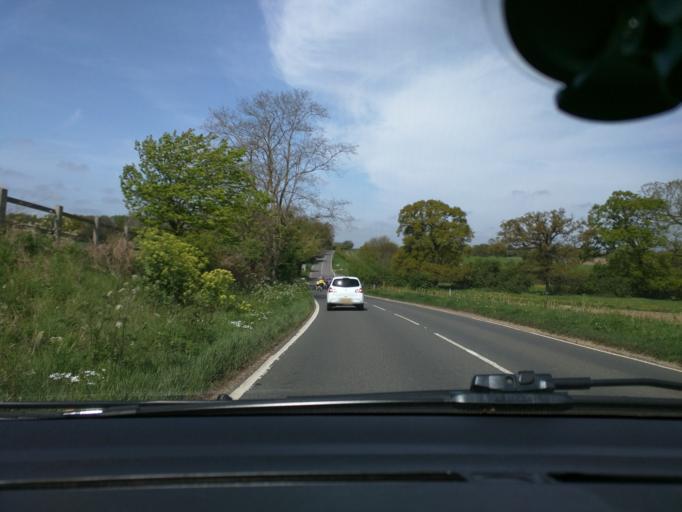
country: GB
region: England
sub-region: Suffolk
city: Leiston
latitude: 52.2428
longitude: 1.5632
